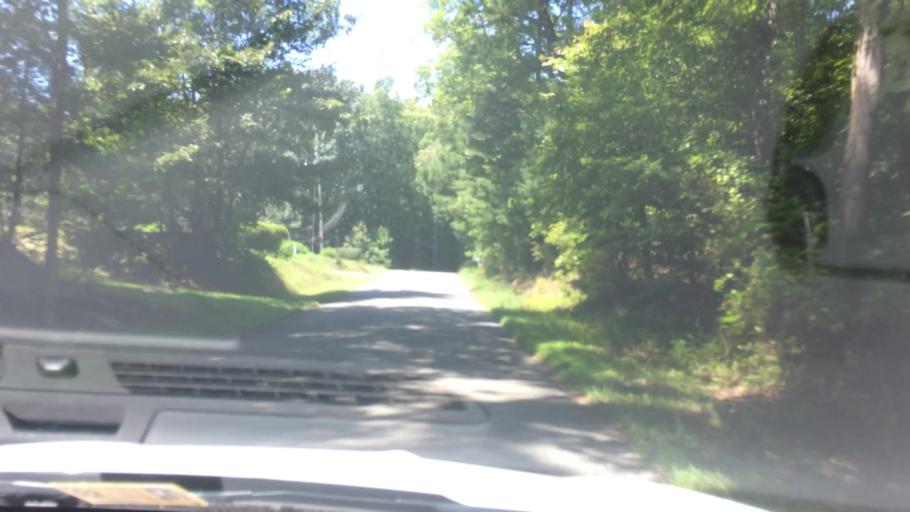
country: US
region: Virginia
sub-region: Charles City County
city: Charles City
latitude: 37.2808
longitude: -76.9300
